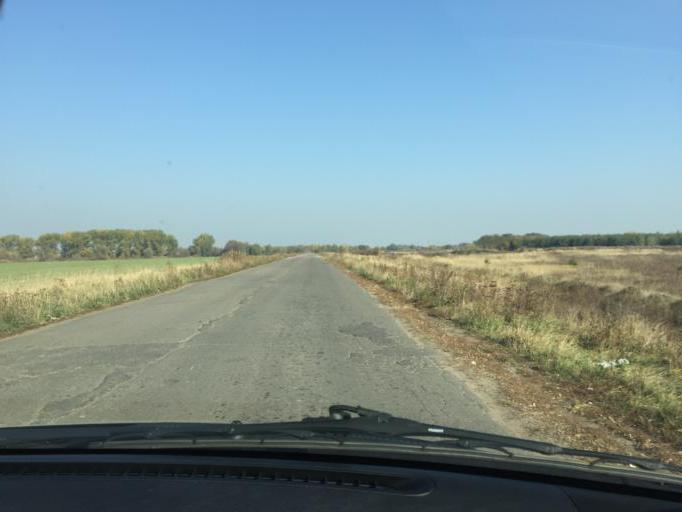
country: BY
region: Brest
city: Davyd-Haradok
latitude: 52.0725
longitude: 27.2423
